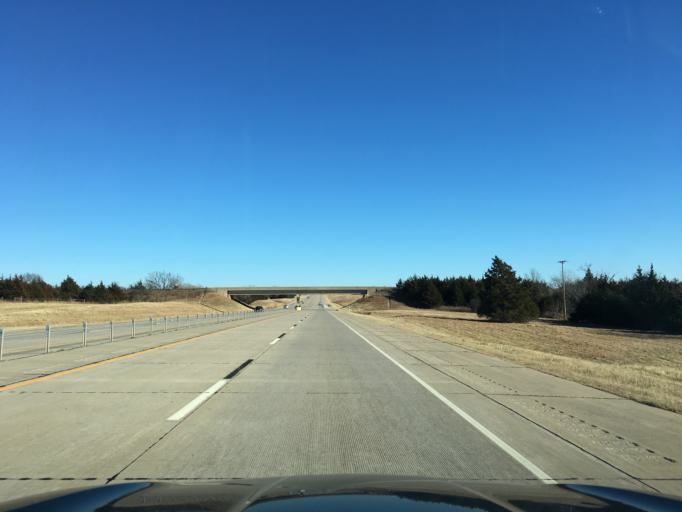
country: US
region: Oklahoma
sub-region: Payne County
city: Yale
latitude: 36.2250
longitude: -96.6804
